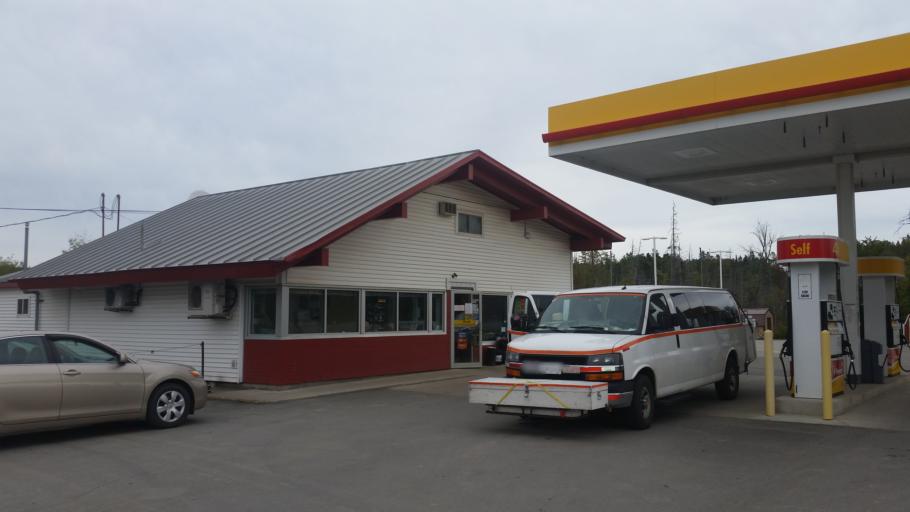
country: US
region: Maine
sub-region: Penobscot County
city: Patten
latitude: 45.8718
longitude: -68.4095
